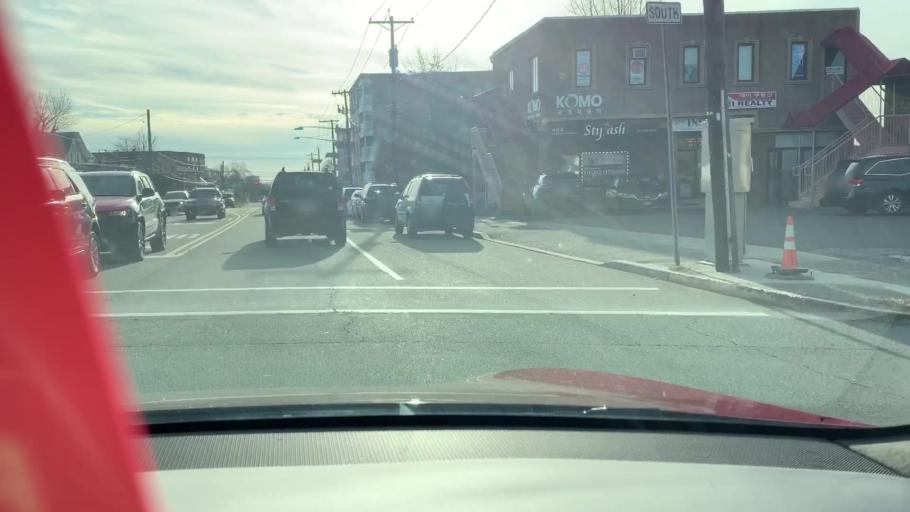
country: US
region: New Jersey
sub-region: Bergen County
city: Palisades Park
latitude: 40.8425
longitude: -73.9877
